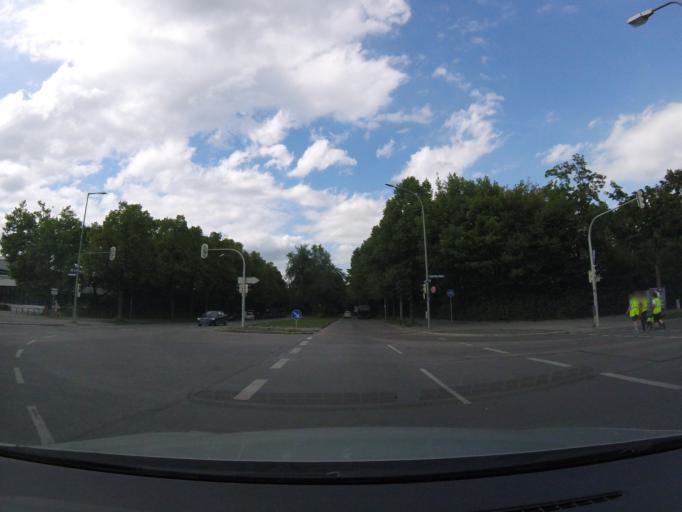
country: DE
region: Bavaria
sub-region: Upper Bavaria
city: Neubiberg
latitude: 48.1088
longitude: 11.6500
